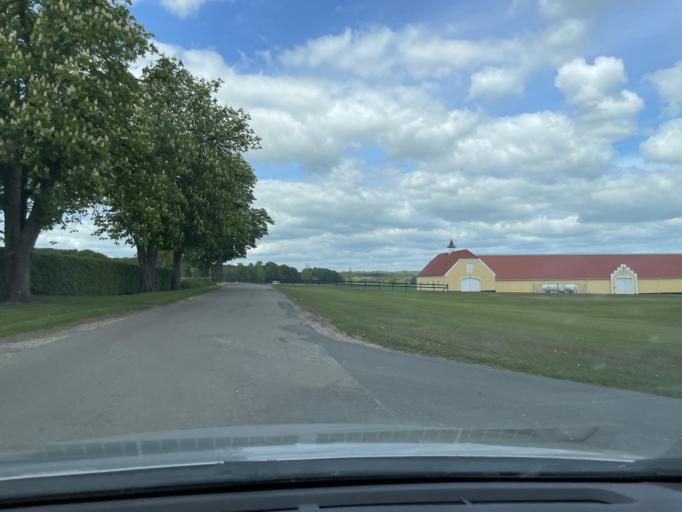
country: DK
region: Central Jutland
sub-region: Odder Kommune
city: Odder
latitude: 55.9112
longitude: 10.1015
